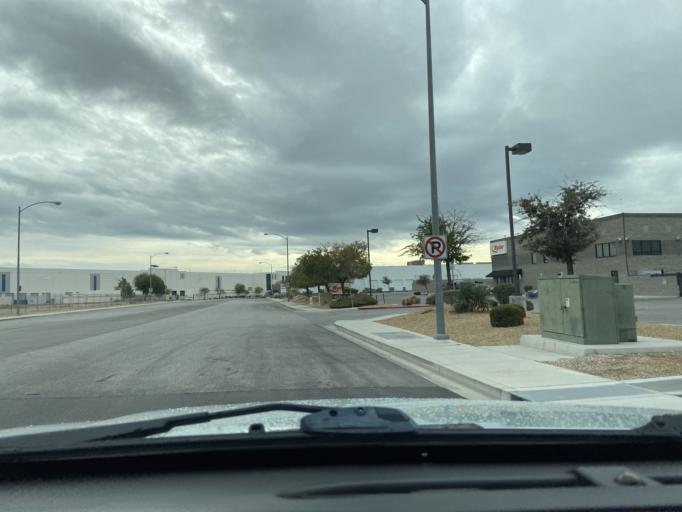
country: US
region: Nevada
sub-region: Clark County
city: North Las Vegas
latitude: 36.2434
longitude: -115.1079
